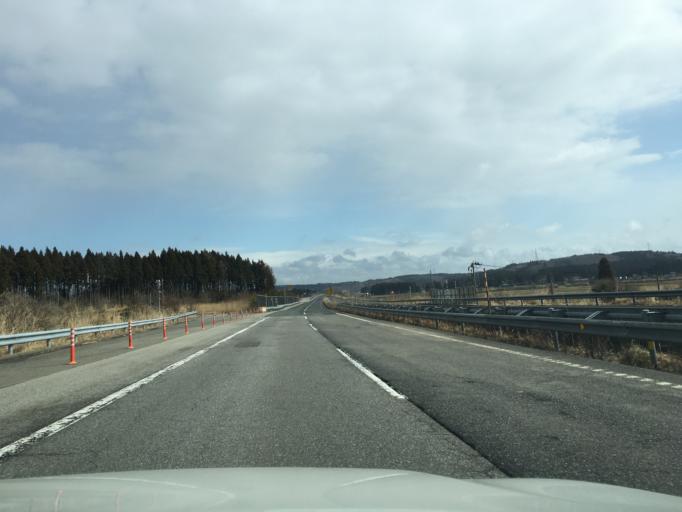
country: JP
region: Akita
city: Akita
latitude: 39.6128
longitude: 140.1412
